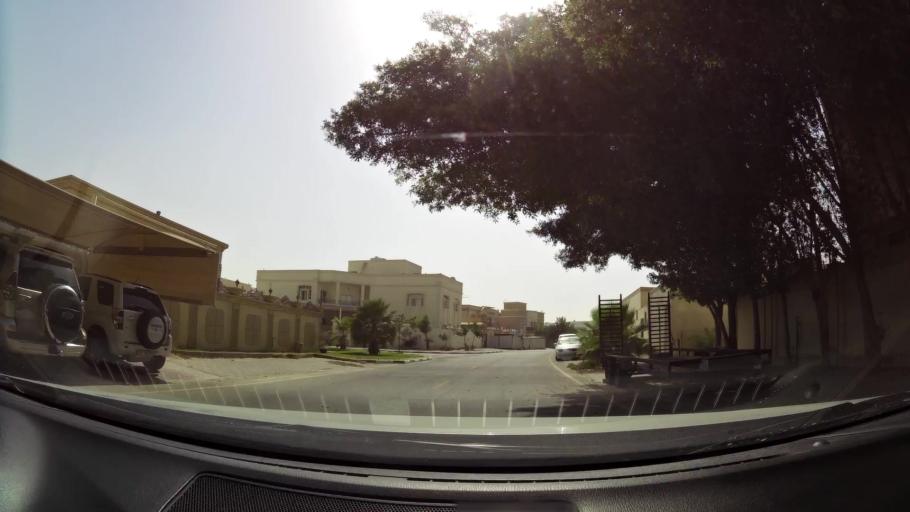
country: AE
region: Dubai
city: Dubai
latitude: 25.1600
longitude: 55.2554
